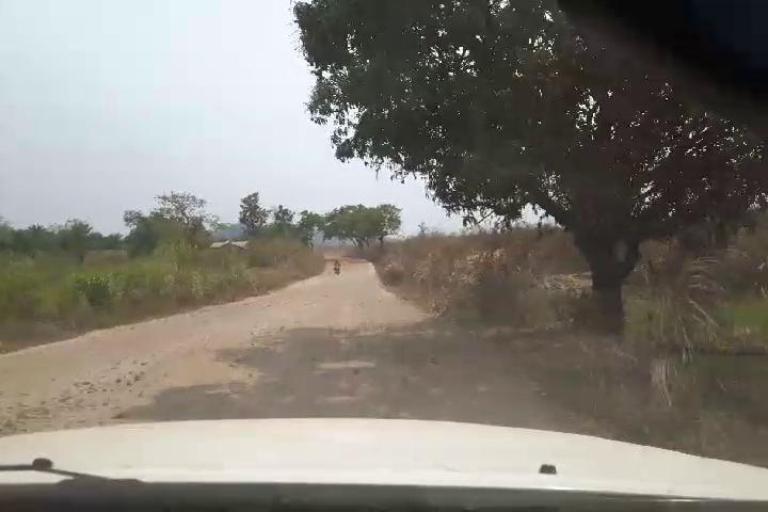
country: SL
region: Northern Province
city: Bumbuna
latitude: 9.0337
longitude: -11.7615
